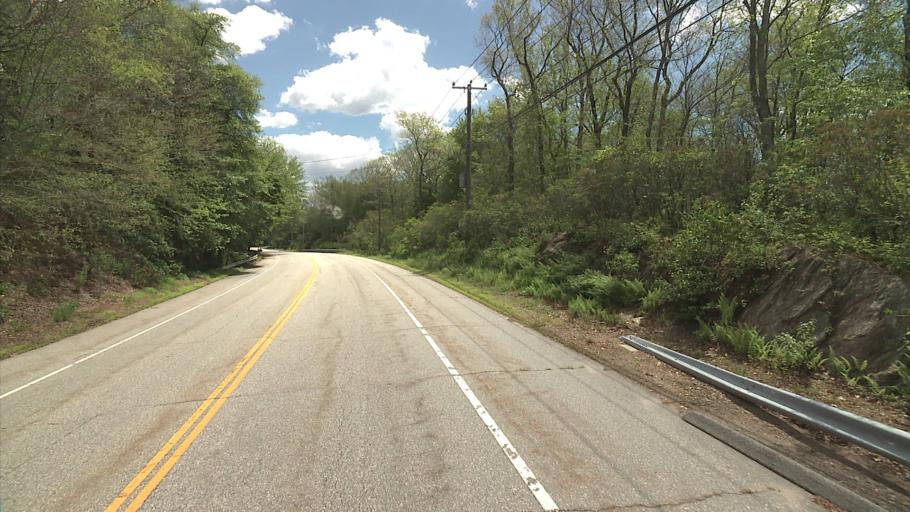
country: US
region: Connecticut
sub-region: Middlesex County
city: Higganum
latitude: 41.5240
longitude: -72.5257
